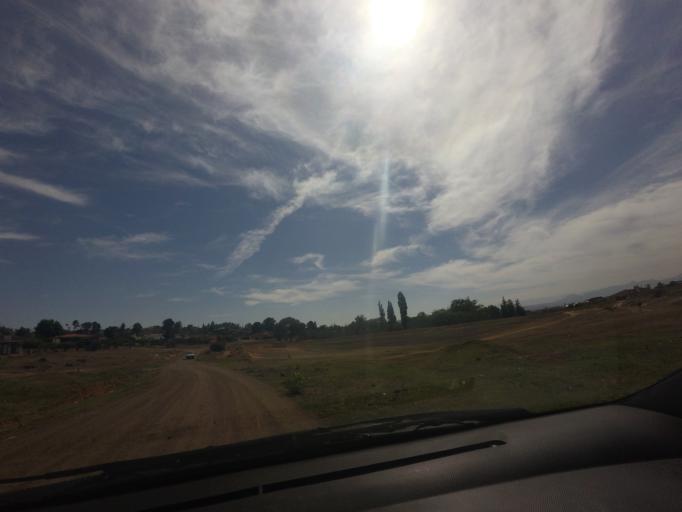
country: LS
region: Berea
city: Teyateyaneng
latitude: -29.1548
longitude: 27.7493
